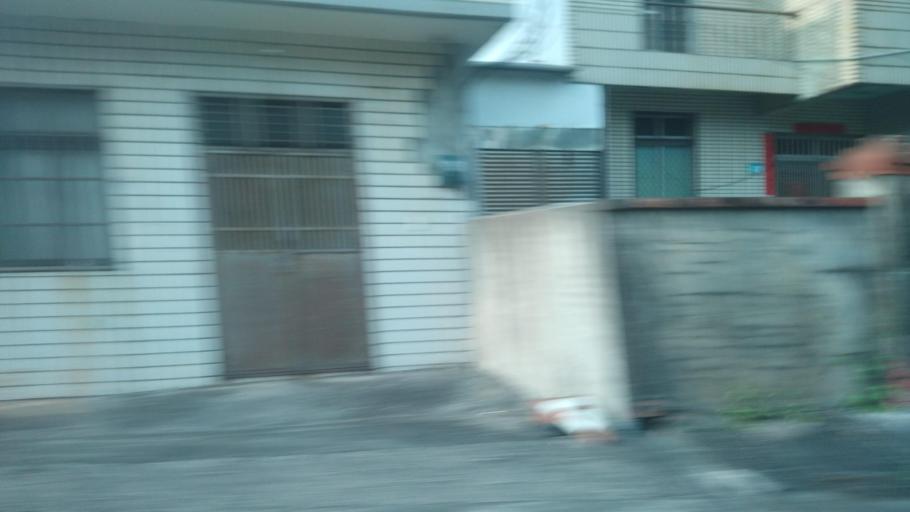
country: TW
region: Taiwan
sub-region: Keelung
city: Keelung
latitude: 25.2802
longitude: 121.6088
